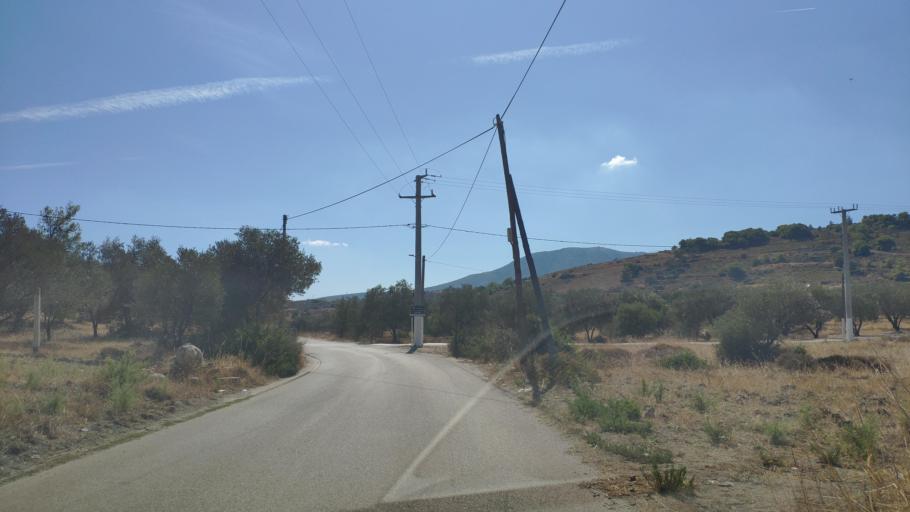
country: GR
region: Attica
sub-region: Nomarchia Anatolikis Attikis
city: Kouvaras
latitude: 37.8284
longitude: 23.9915
